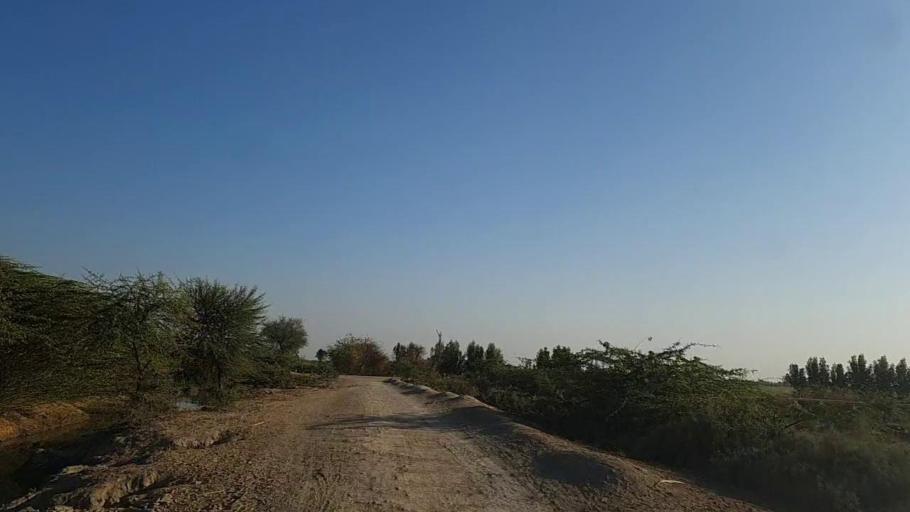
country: PK
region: Sindh
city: Samaro
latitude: 25.3323
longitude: 69.4127
